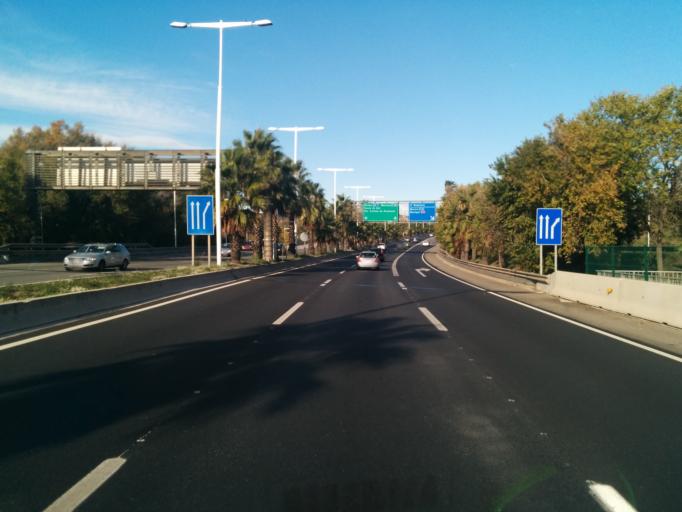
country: ES
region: Catalonia
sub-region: Provincia de Barcelona
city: Sant Adria de Besos
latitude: 41.4217
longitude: 2.2210
